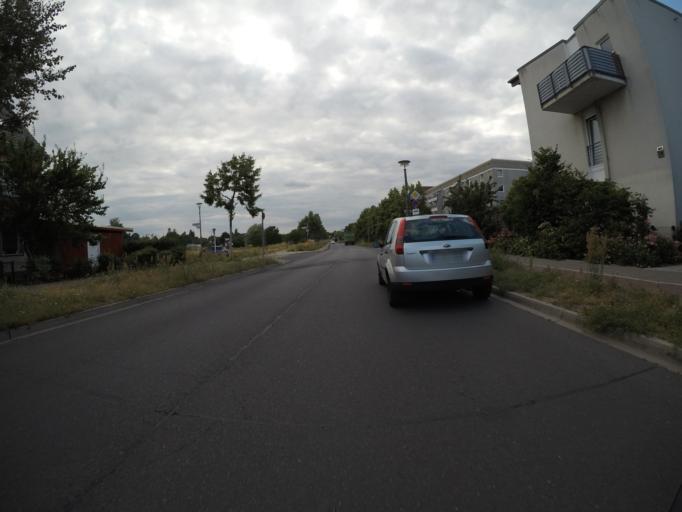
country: DE
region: Berlin
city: Mahlsdorf
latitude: 52.5186
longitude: 13.6039
